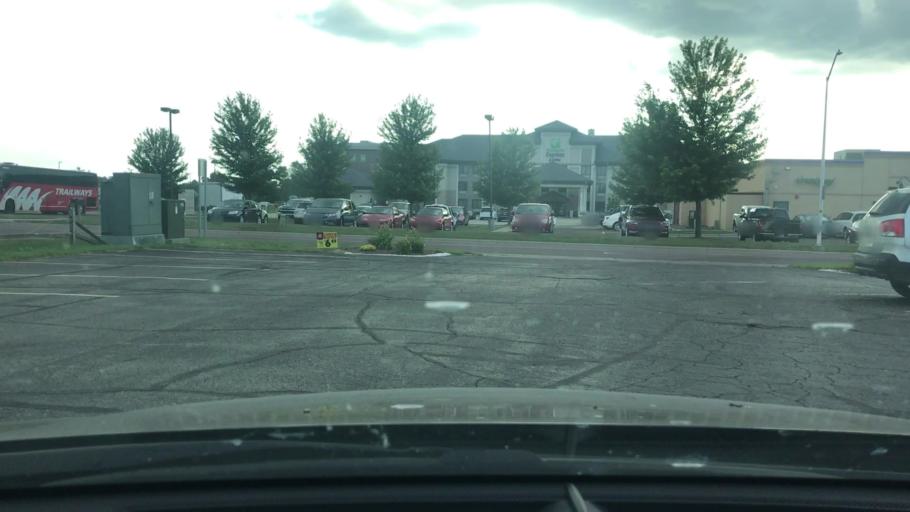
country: US
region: Minnesota
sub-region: Nobles County
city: Worthington
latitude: 43.6353
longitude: -95.5917
